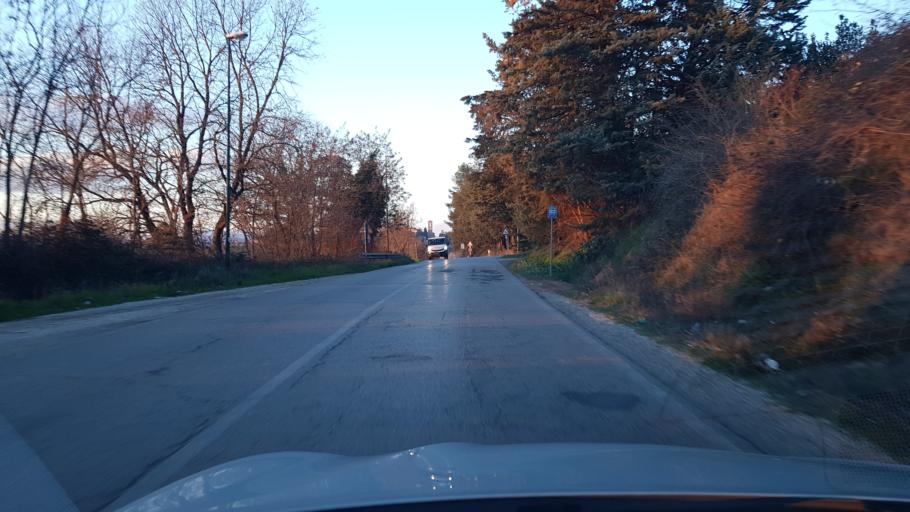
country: IT
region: Umbria
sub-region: Provincia di Perugia
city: Torgiano
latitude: 43.0141
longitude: 12.4361
